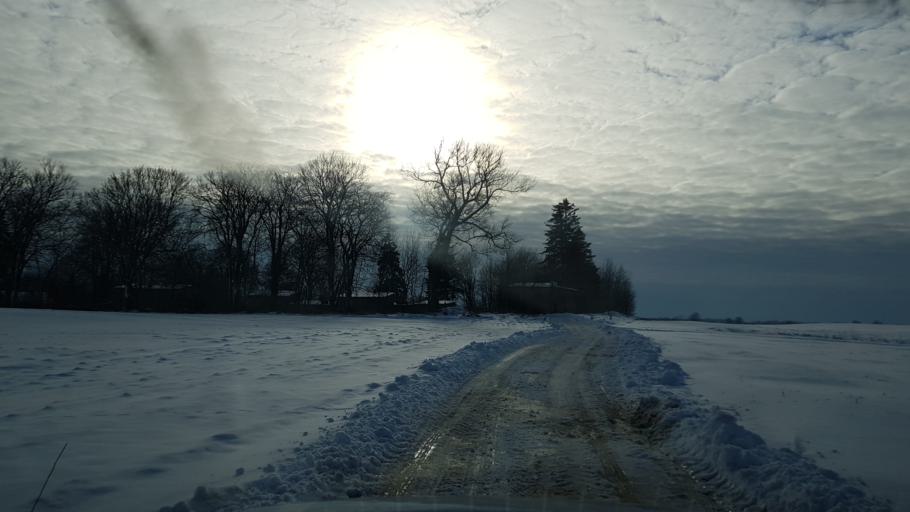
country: PL
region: West Pomeranian Voivodeship
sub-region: Powiat drawski
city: Drawsko Pomorskie
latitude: 53.5369
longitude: 15.7735
